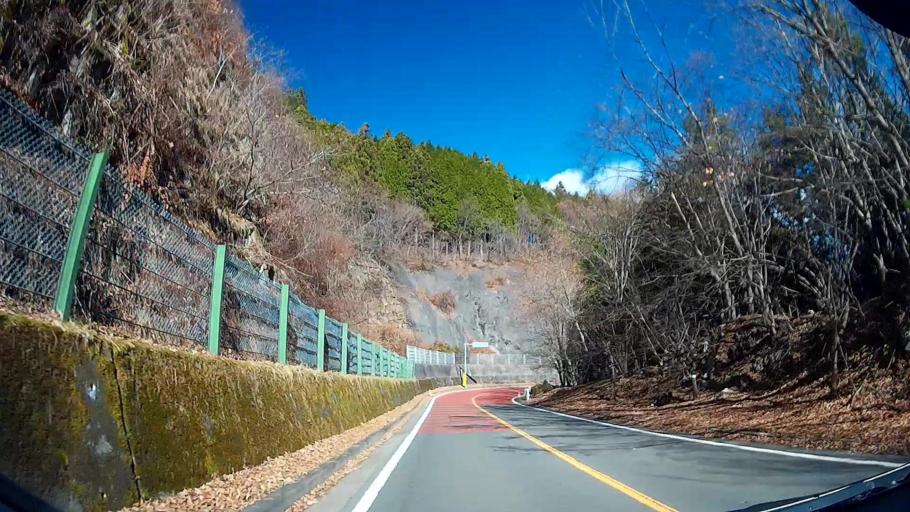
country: JP
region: Yamanashi
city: Uenohara
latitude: 35.7566
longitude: 139.0432
